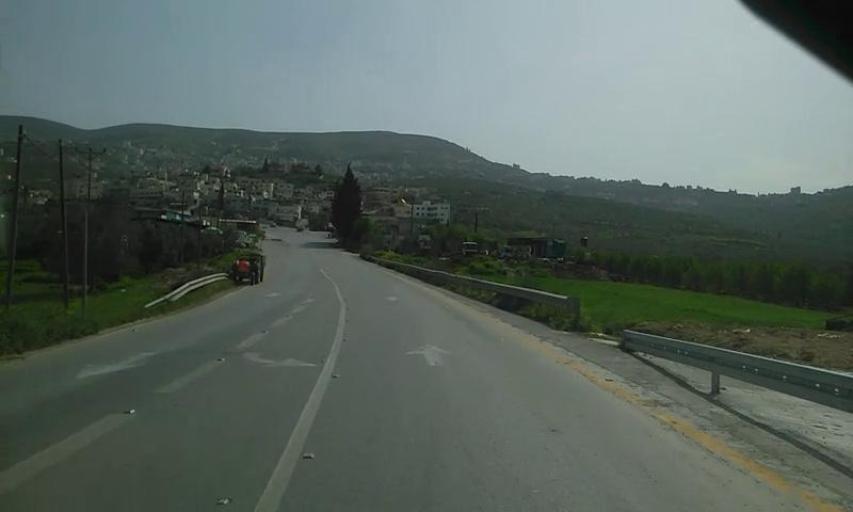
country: PS
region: West Bank
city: Al Fandaqumiyah
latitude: 32.3336
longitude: 35.2048
